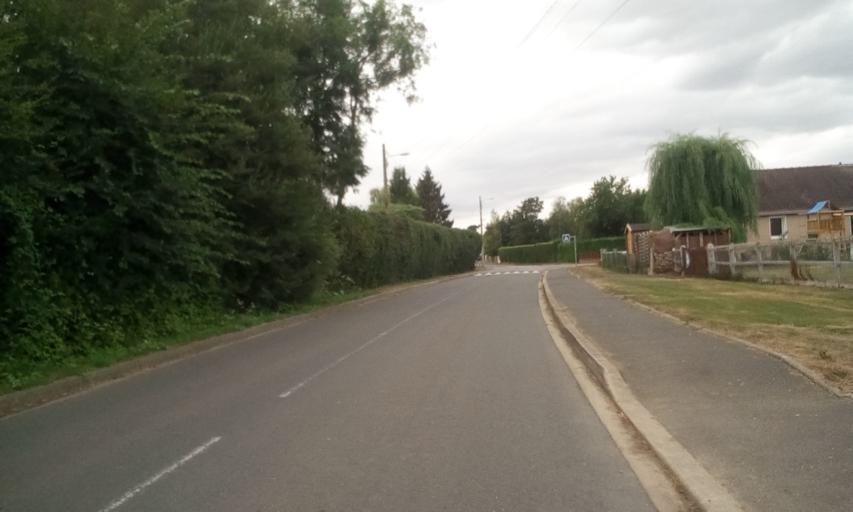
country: FR
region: Lower Normandy
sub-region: Departement du Calvados
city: Bellengreville
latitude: 49.1490
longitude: -0.2234
